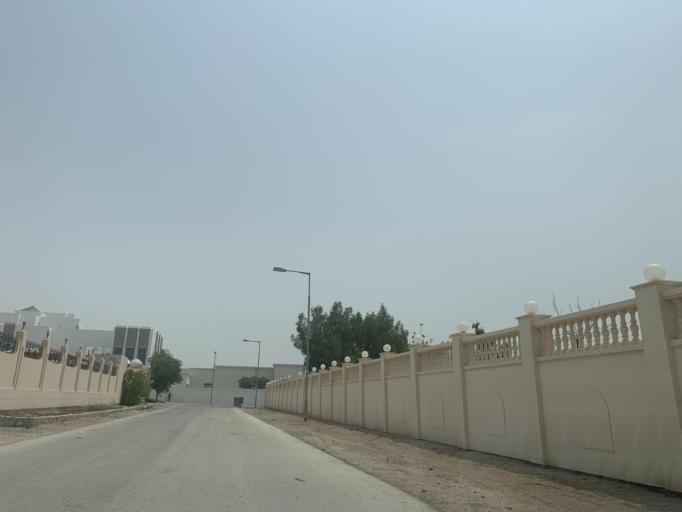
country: BH
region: Central Governorate
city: Madinat Hamad
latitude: 26.1613
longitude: 50.4787
